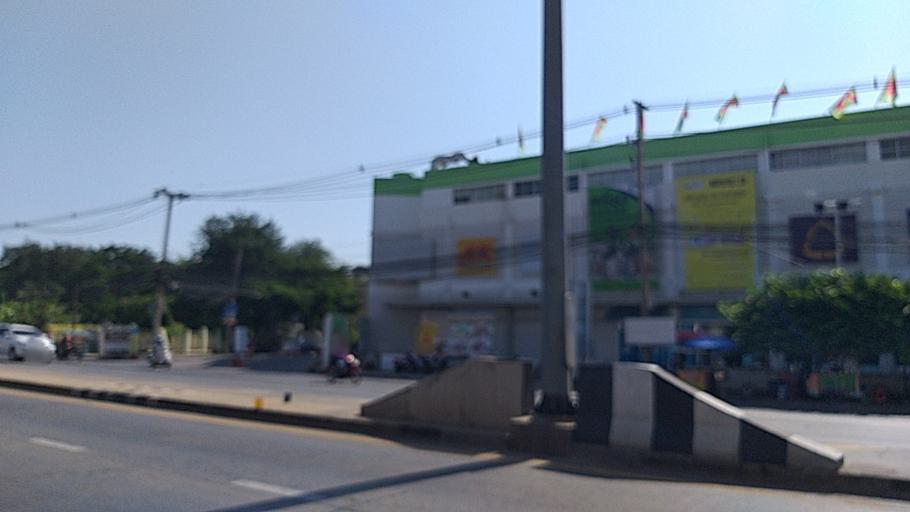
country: TH
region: Nakhon Ratchasima
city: Nakhon Ratchasima
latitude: 14.9822
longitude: 102.0914
